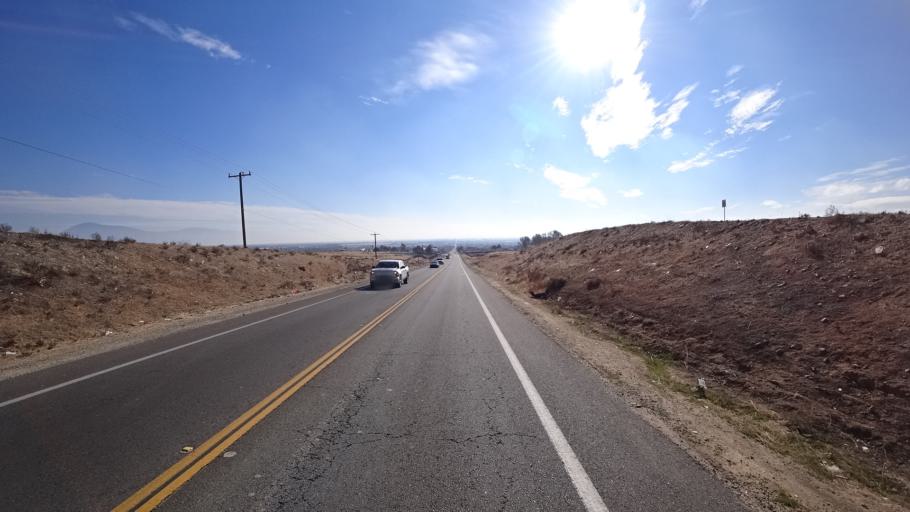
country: US
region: California
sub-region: Kern County
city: Bakersfield
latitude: 35.3870
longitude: -118.9145
